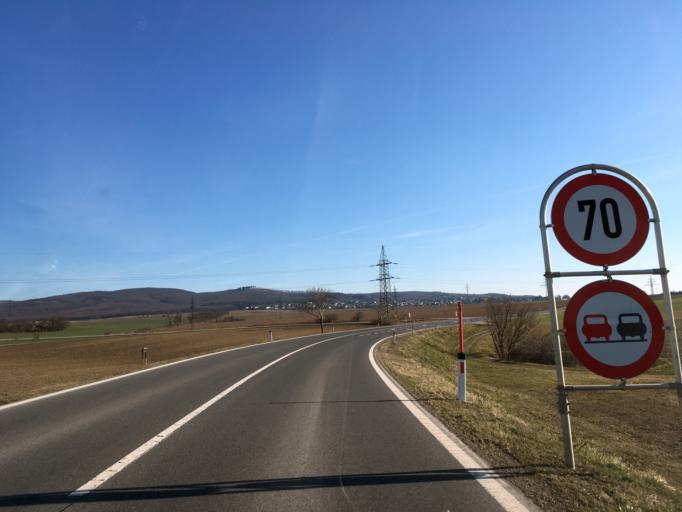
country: AT
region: Burgenland
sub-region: Eisenstadt-Umgebung
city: Wimpassing an der Leitha
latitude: 47.9025
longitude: 16.4372
